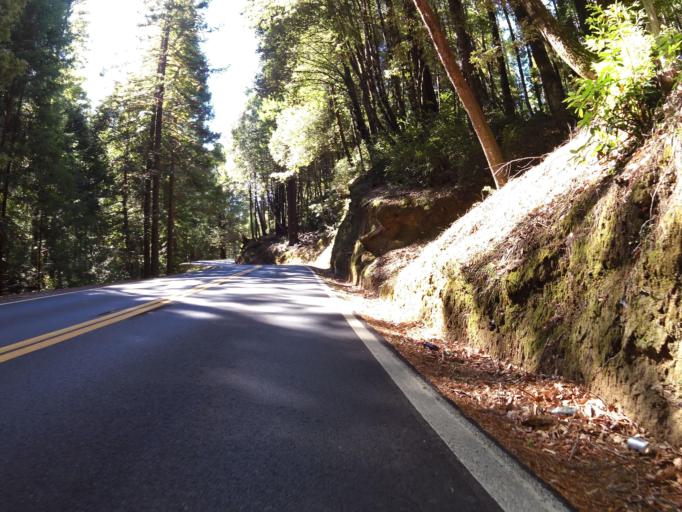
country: US
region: California
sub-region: Humboldt County
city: Redway
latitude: 39.8513
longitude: -123.7299
